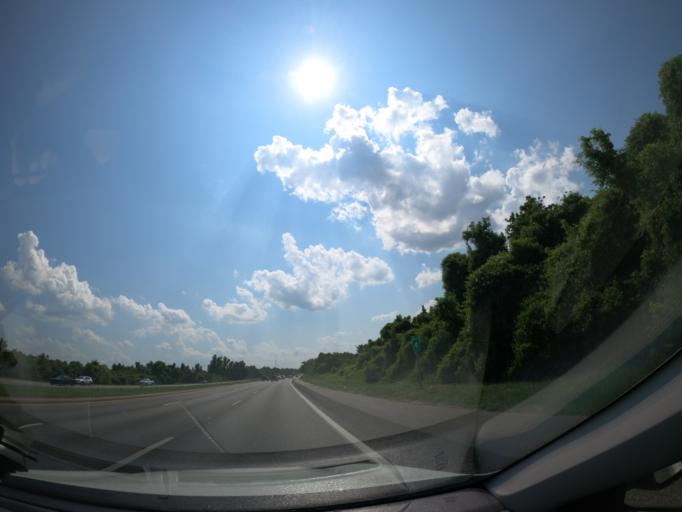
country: US
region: South Carolina
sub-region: Richland County
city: Columbia
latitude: 33.9366
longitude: -81.0092
